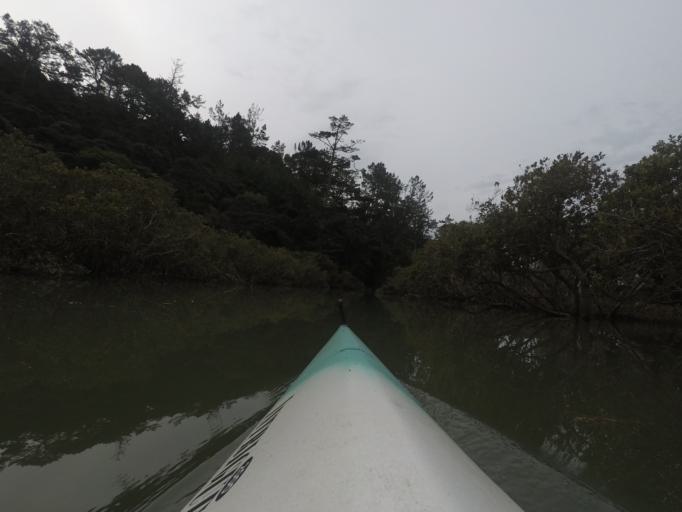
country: NZ
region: Auckland
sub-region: Auckland
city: Rothesay Bay
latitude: -36.6803
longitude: 174.7058
